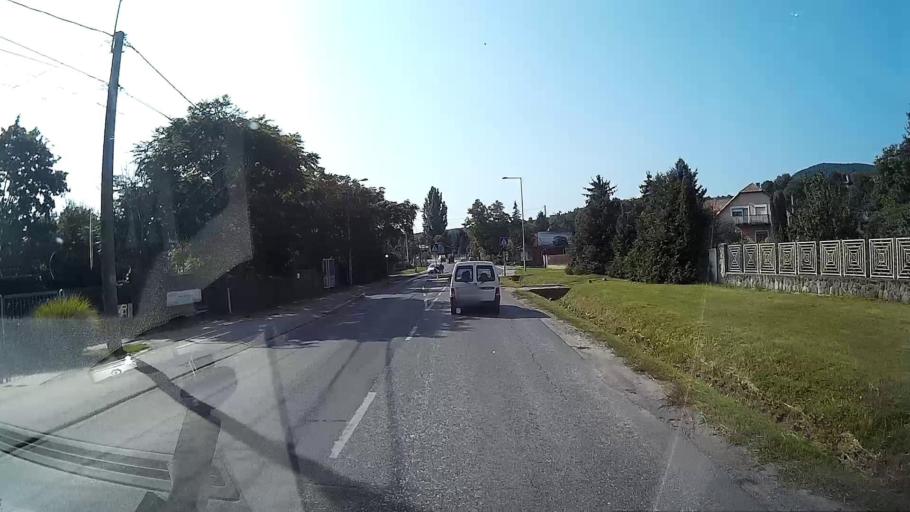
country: HU
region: Pest
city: Tahitotfalu
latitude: 47.7469
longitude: 19.0820
